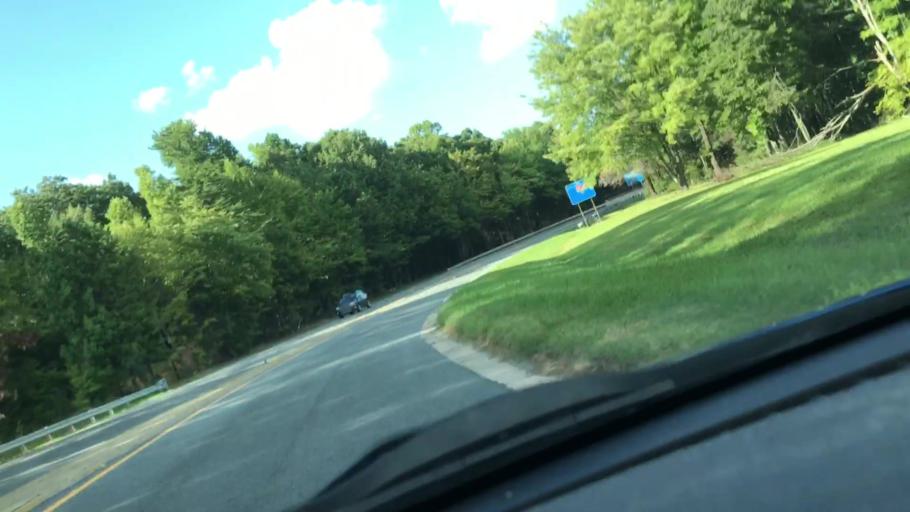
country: US
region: North Carolina
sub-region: Randolph County
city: Asheboro
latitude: 35.7305
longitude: -79.8255
